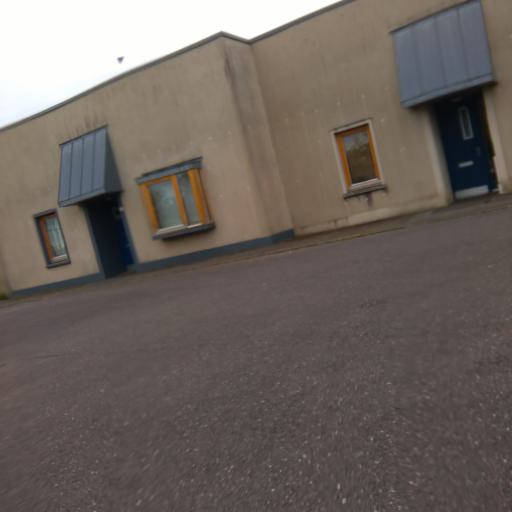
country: IE
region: Munster
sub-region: County Cork
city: Cork
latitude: 51.9130
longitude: -8.4589
